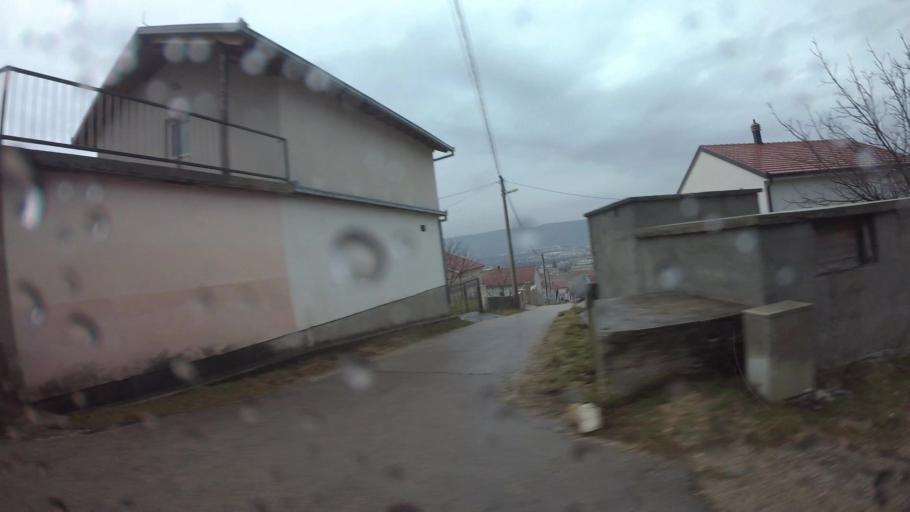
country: BA
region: Federation of Bosnia and Herzegovina
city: Rodoc
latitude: 43.3070
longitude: 17.8447
